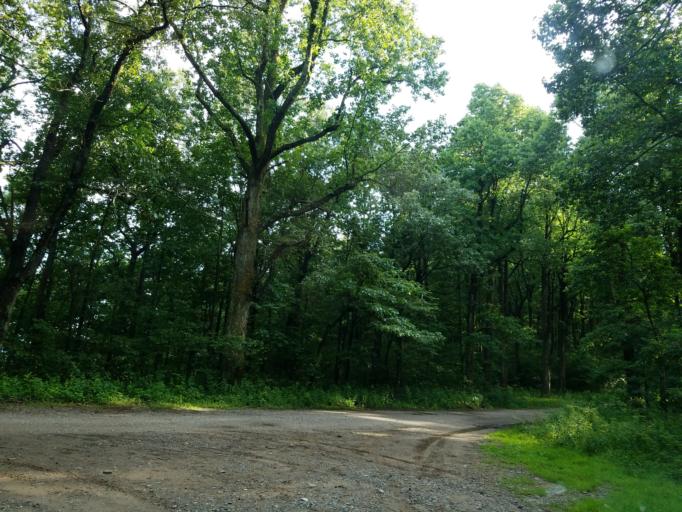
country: US
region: Georgia
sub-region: Lumpkin County
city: Dahlonega
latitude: 34.6526
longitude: -84.1379
